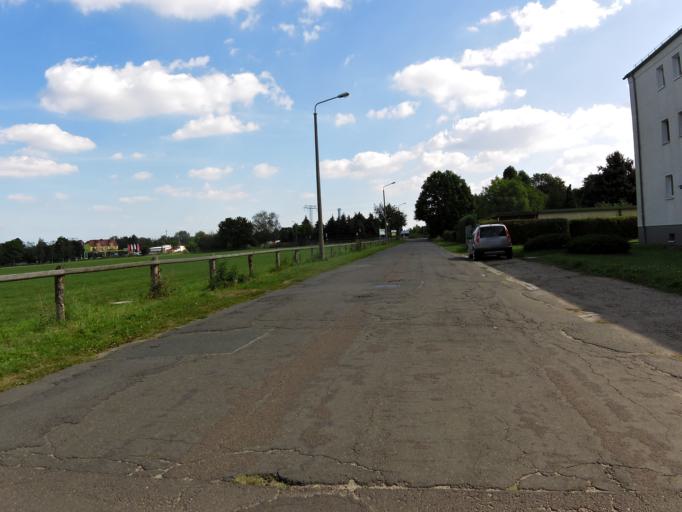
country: DE
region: Saxony
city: Leipzig
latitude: 51.3691
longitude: 12.4229
